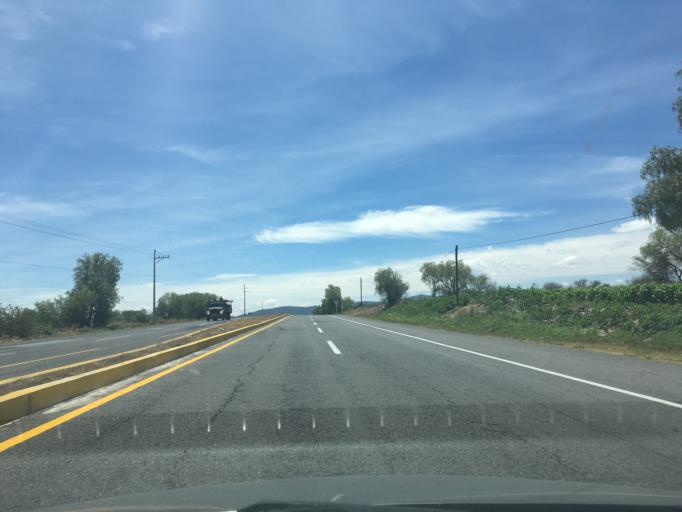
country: MX
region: Hidalgo
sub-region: Alfajayucan
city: Santa Maria Xigui
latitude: 20.4347
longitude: -99.4048
